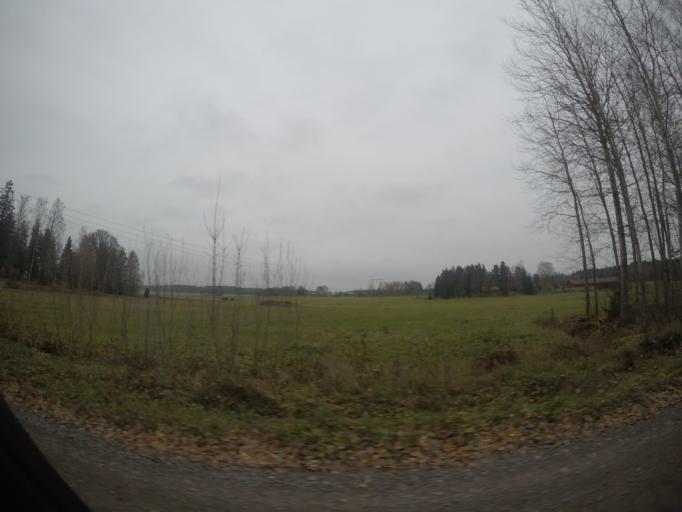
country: SE
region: Vaestmanland
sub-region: Kopings Kommun
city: Koping
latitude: 59.5934
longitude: 16.0847
